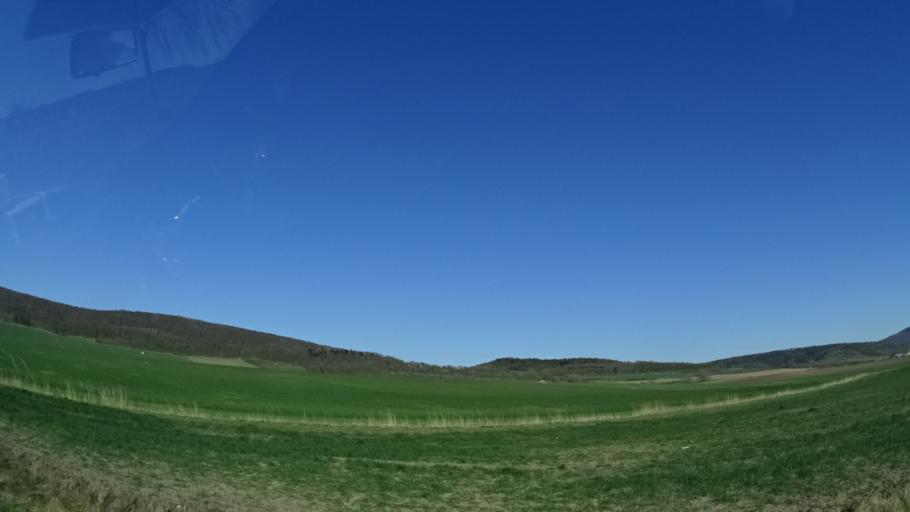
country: DE
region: Thuringia
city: Romhild
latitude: 50.4268
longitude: 10.5117
